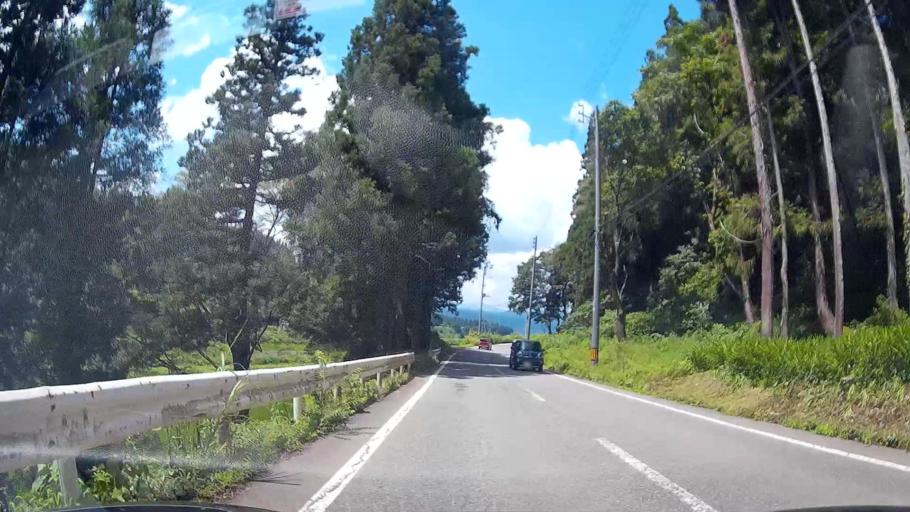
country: JP
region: Niigata
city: Tokamachi
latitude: 37.0775
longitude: 138.7552
